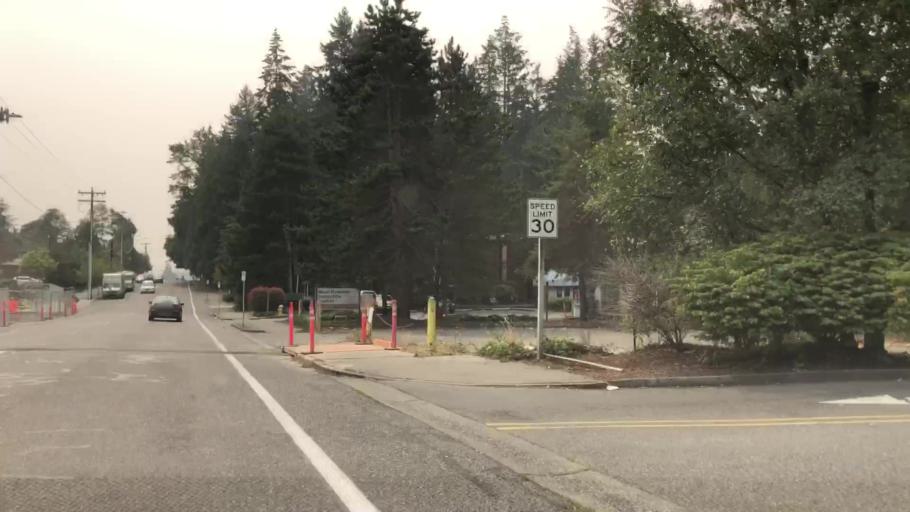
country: US
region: Washington
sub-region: Snohomish County
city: Lynnwood
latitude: 47.8205
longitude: -122.3197
